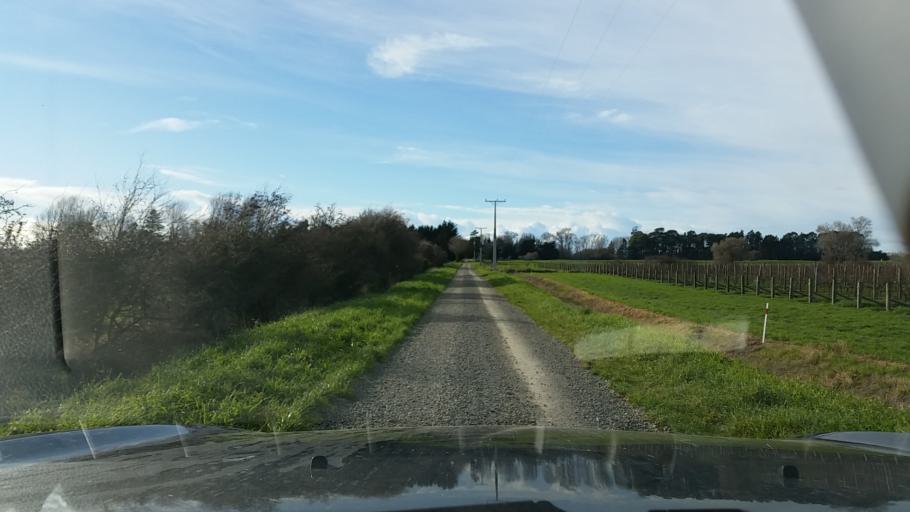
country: NZ
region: Marlborough
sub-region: Marlborough District
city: Blenheim
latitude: -41.4308
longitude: 173.9898
